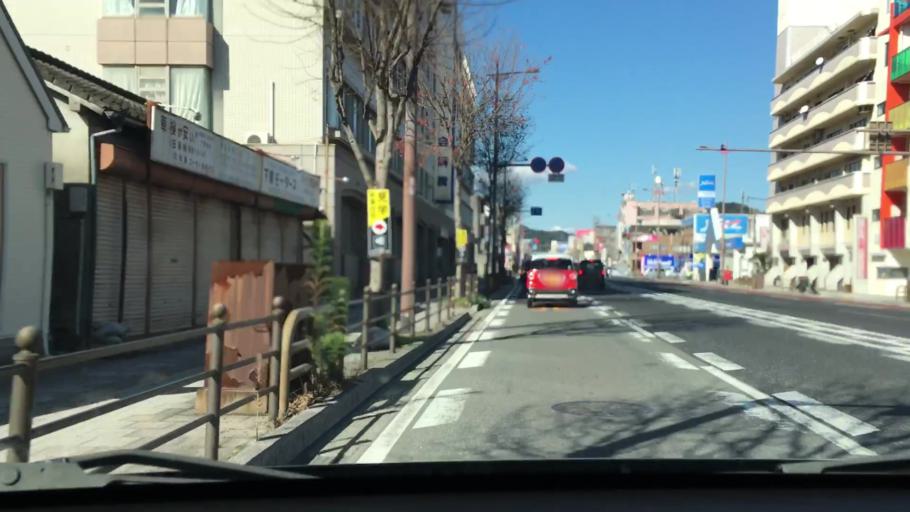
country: JP
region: Kagoshima
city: Kagoshima-shi
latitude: 31.6084
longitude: 130.5353
